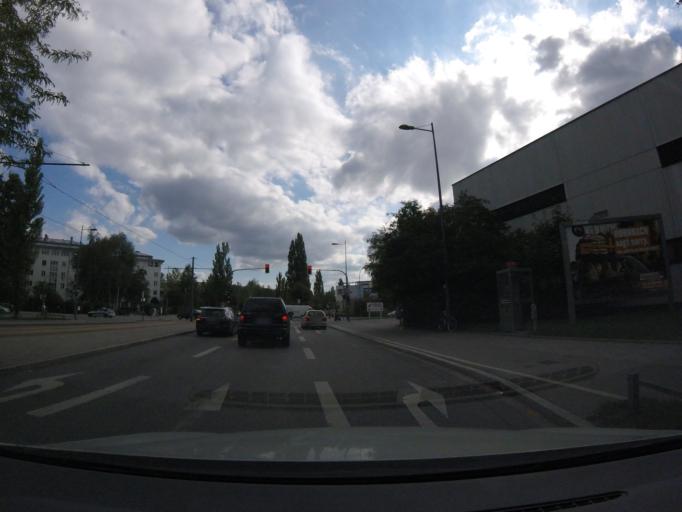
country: DE
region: Bavaria
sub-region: Upper Bavaria
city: Unterfoehring
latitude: 48.1698
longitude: 11.6348
